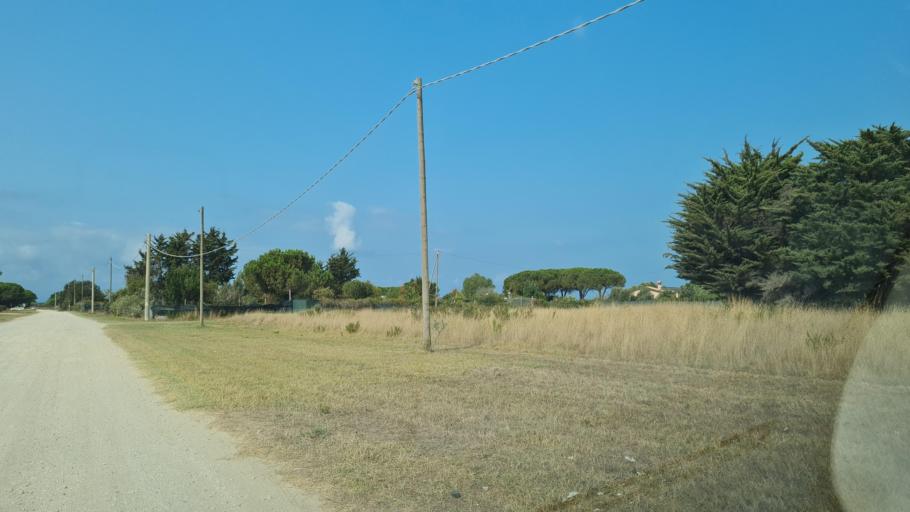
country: IT
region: Latium
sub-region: Provincia di Viterbo
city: Tarquinia
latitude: 42.1922
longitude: 11.7293
